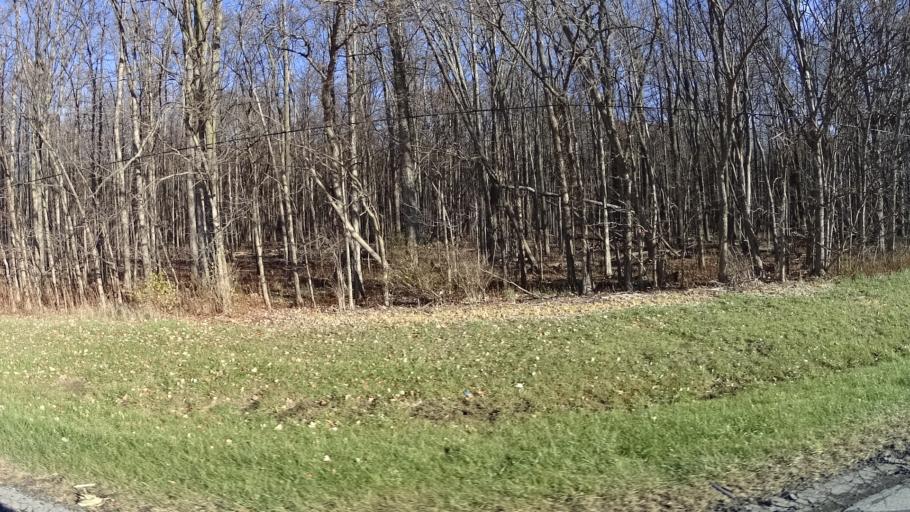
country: US
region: Ohio
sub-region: Lorain County
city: Wellington
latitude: 41.1295
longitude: -82.2192
